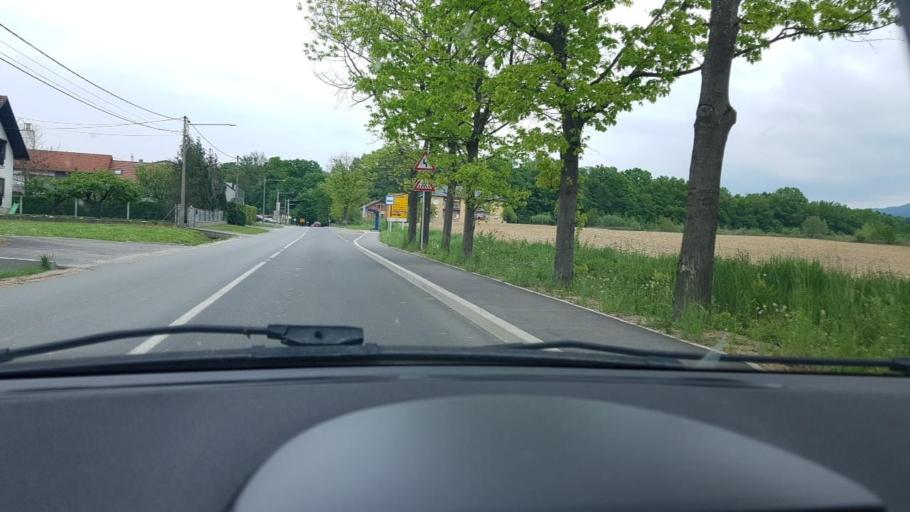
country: HR
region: Krapinsko-Zagorska
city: Bedekovcina
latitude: 45.9801
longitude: 15.9843
